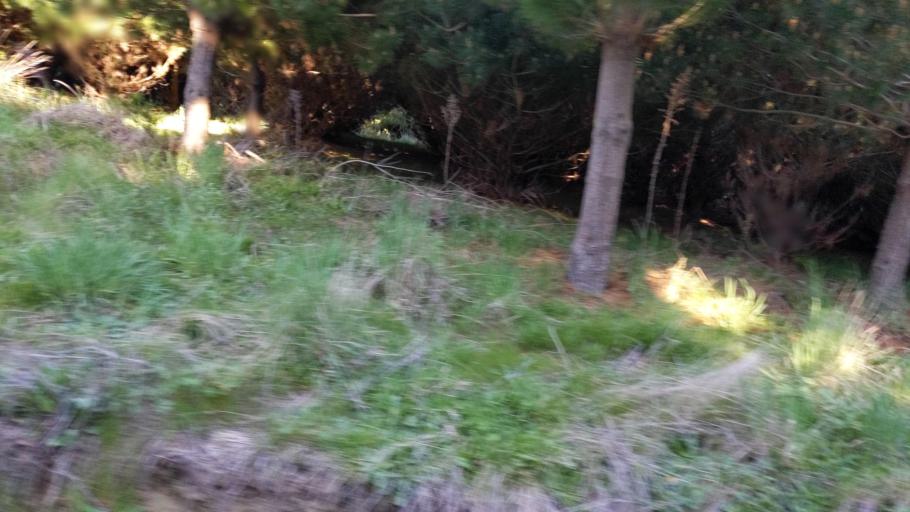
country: AU
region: New South Wales
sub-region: Blayney
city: Millthorpe
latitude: -33.3983
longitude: 149.3137
